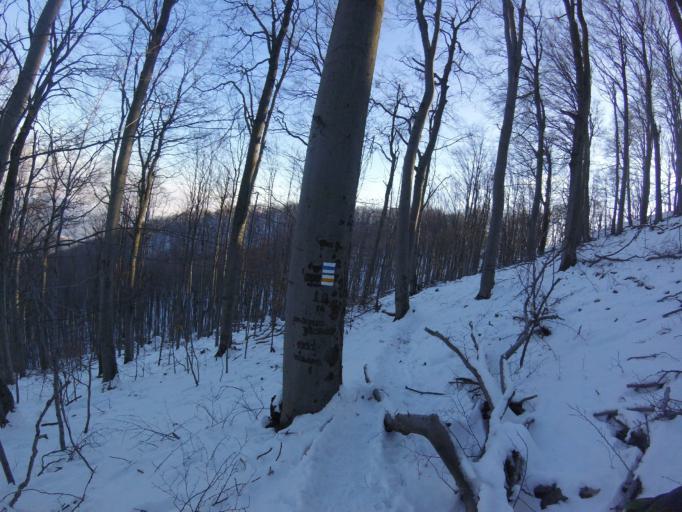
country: HU
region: Heves
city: Parad
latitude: 47.8756
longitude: 20.0357
